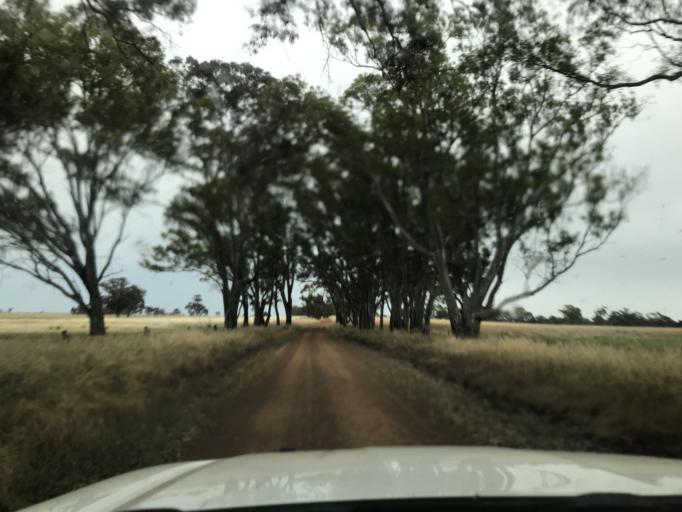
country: AU
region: Victoria
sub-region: Horsham
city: Horsham
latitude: -37.0667
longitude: 141.6725
